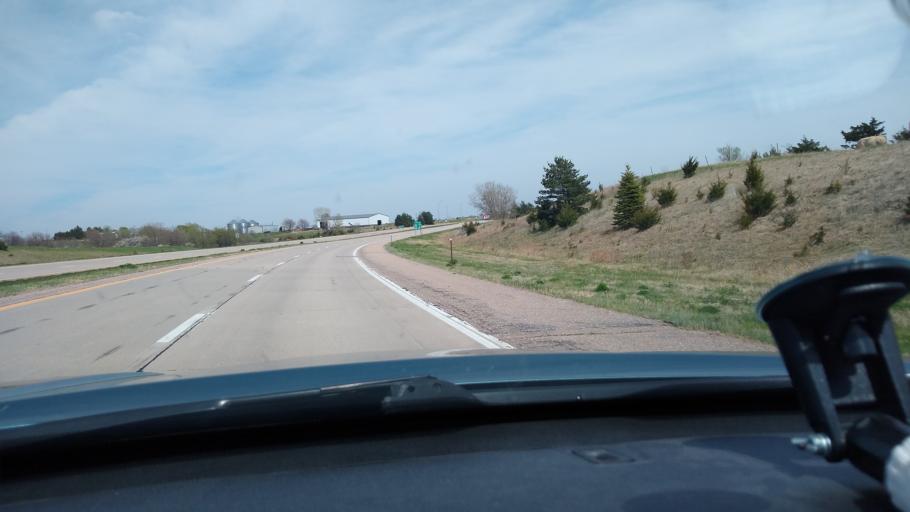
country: US
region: Nebraska
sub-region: Thayer County
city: Hebron
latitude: 40.1372
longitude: -97.6005
